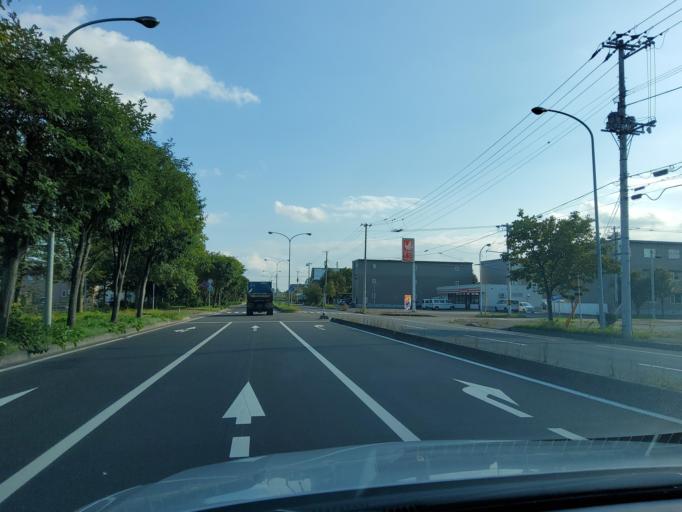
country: JP
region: Hokkaido
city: Obihiro
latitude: 42.9061
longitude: 143.2139
